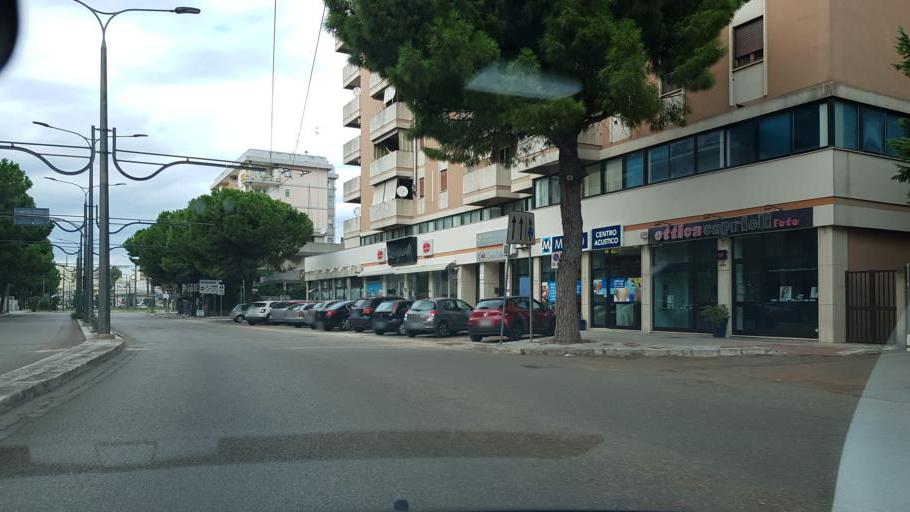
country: IT
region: Apulia
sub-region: Provincia di Lecce
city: Lecce
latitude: 40.3573
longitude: 18.1840
